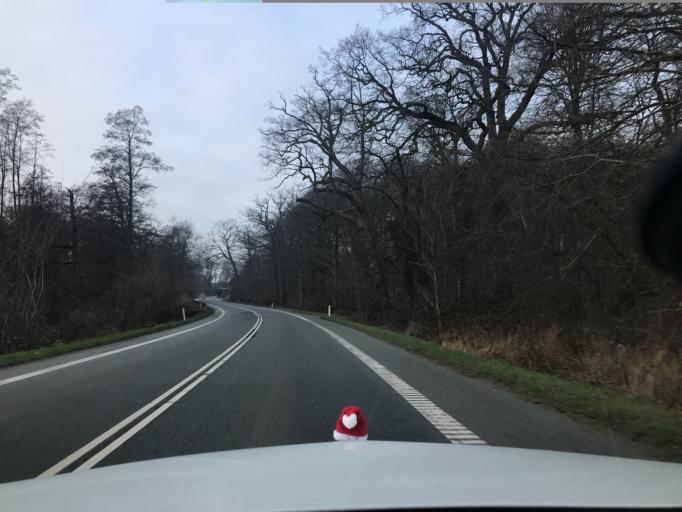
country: DK
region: South Denmark
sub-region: Sonderborg Kommune
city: Grasten
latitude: 54.9288
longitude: 9.5937
